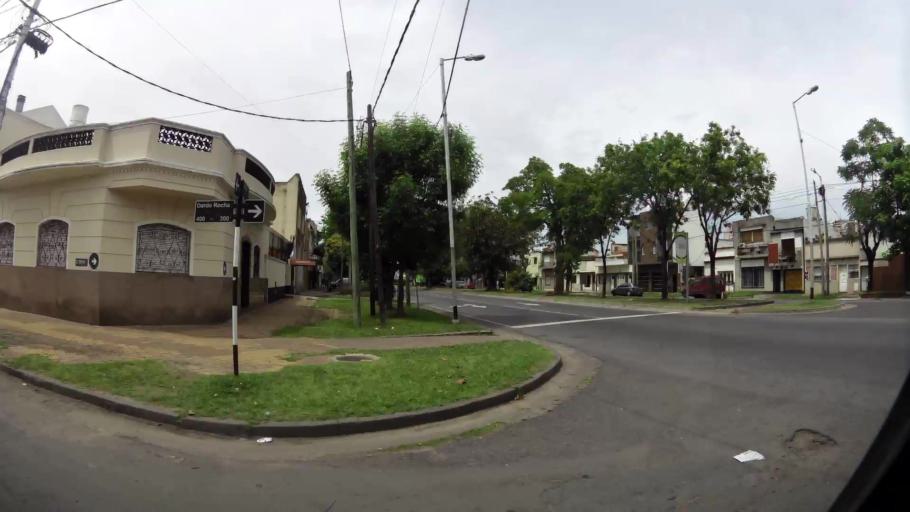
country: AR
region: Buenos Aires
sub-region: Partido de Avellaneda
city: Avellaneda
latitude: -34.6660
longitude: -58.3524
